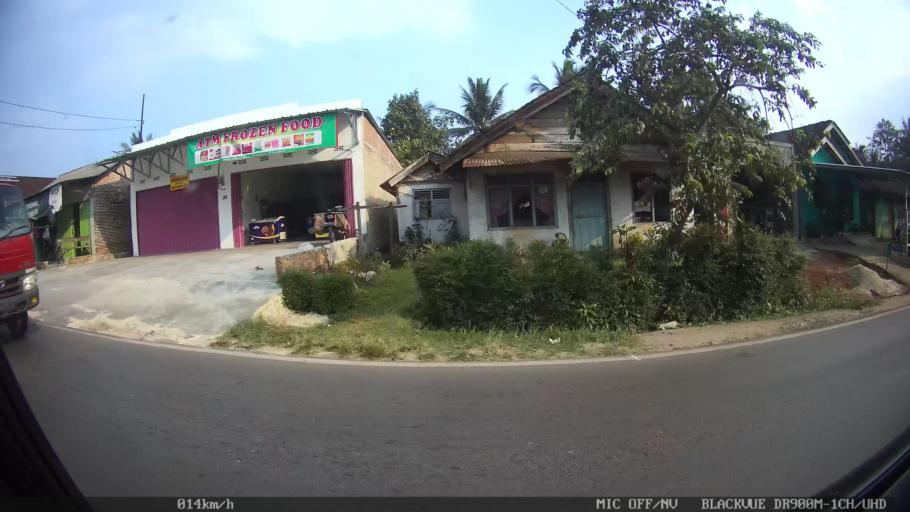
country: ID
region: Lampung
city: Natar
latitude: -5.3641
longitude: 105.1849
